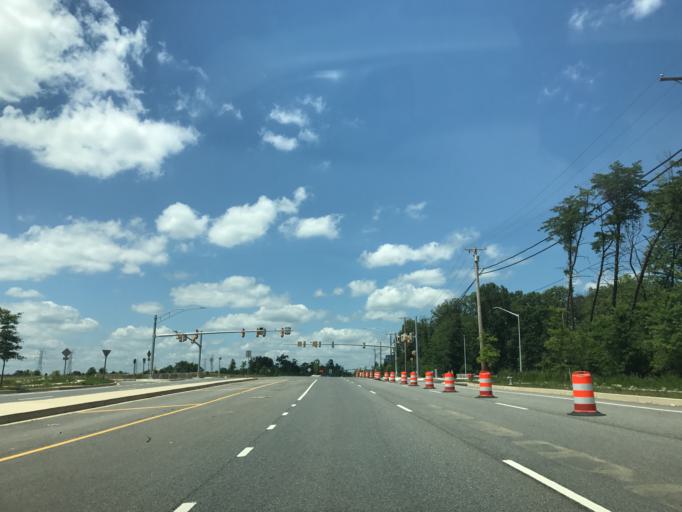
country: US
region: Maryland
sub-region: Prince George's County
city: West Laurel
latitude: 39.0781
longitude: -76.8866
